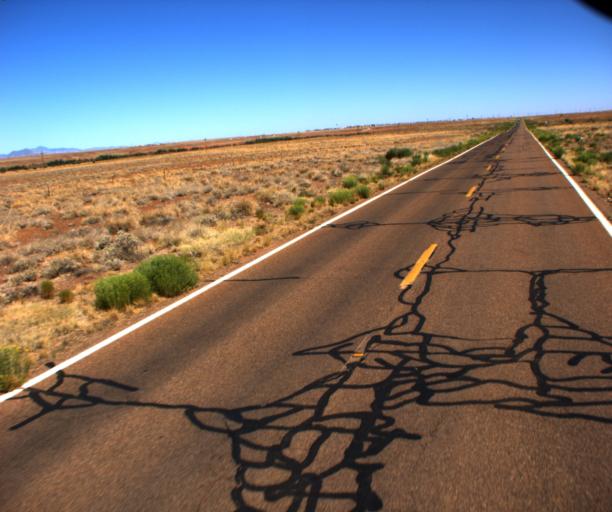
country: US
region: Arizona
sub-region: Coconino County
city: LeChee
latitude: 35.2697
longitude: -110.9744
